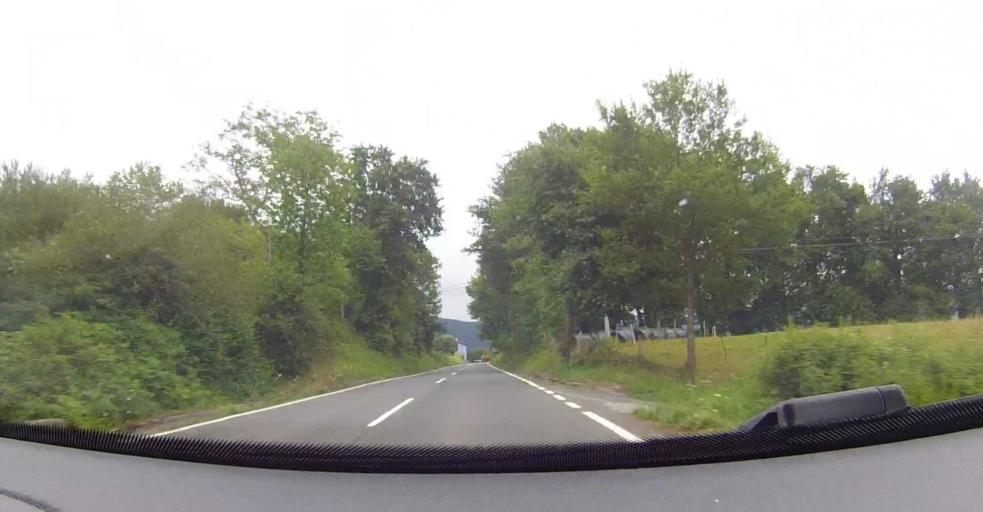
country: ES
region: Basque Country
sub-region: Bizkaia
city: Lanestosa
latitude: 43.2396
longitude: -3.3194
